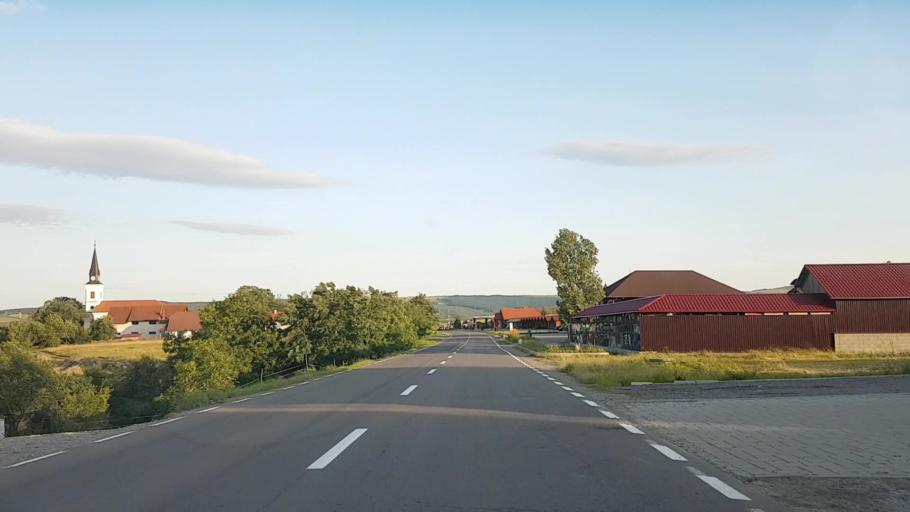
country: RO
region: Harghita
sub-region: Comuna Lupeni
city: Lupeni
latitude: 46.3794
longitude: 25.2193
